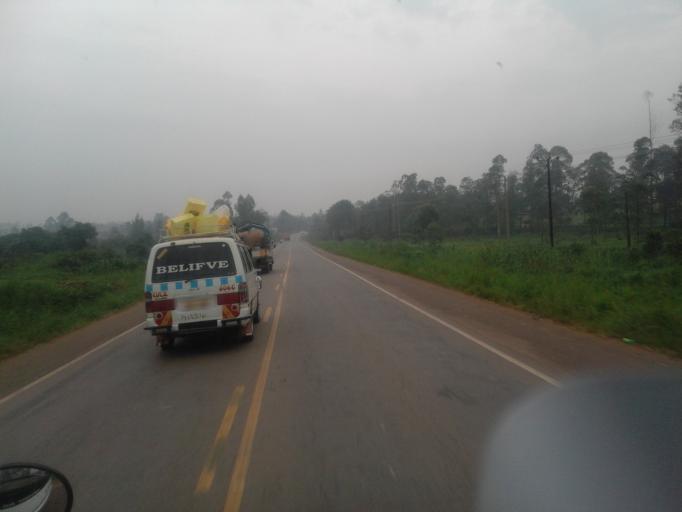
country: UG
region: Central Region
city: Lugazi
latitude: 0.3752
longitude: 32.9132
